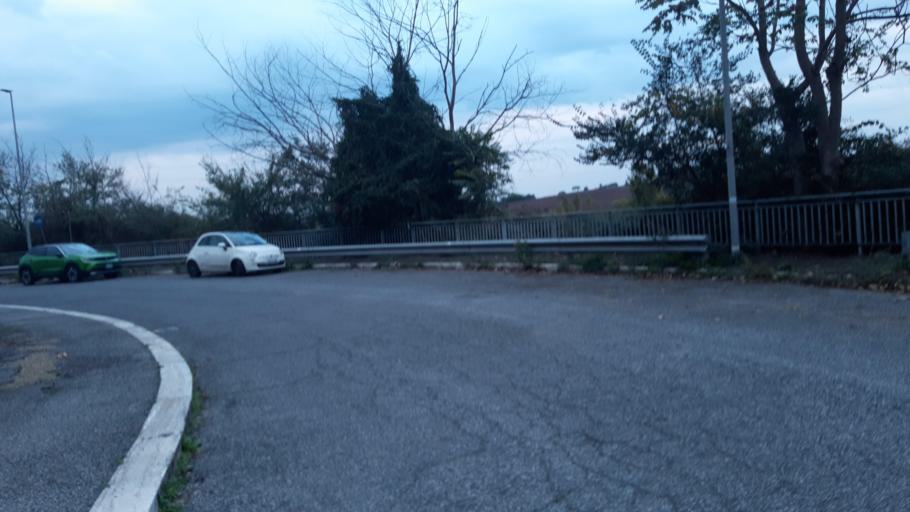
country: VA
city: Vatican City
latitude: 41.9669
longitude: 12.4066
